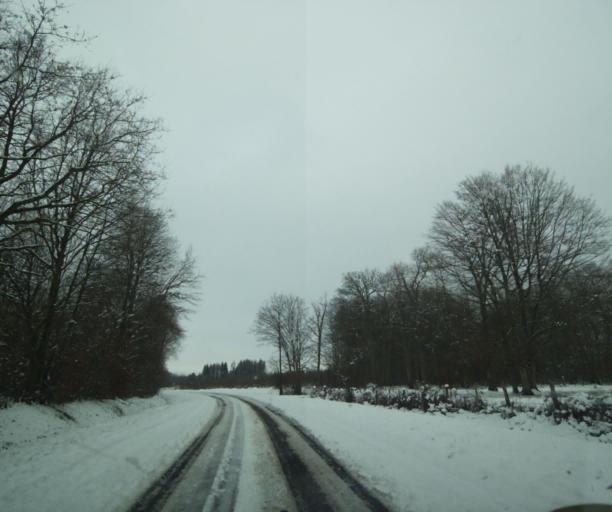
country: FR
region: Champagne-Ardenne
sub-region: Departement de la Haute-Marne
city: Montier-en-Der
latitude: 48.4823
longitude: 4.6779
